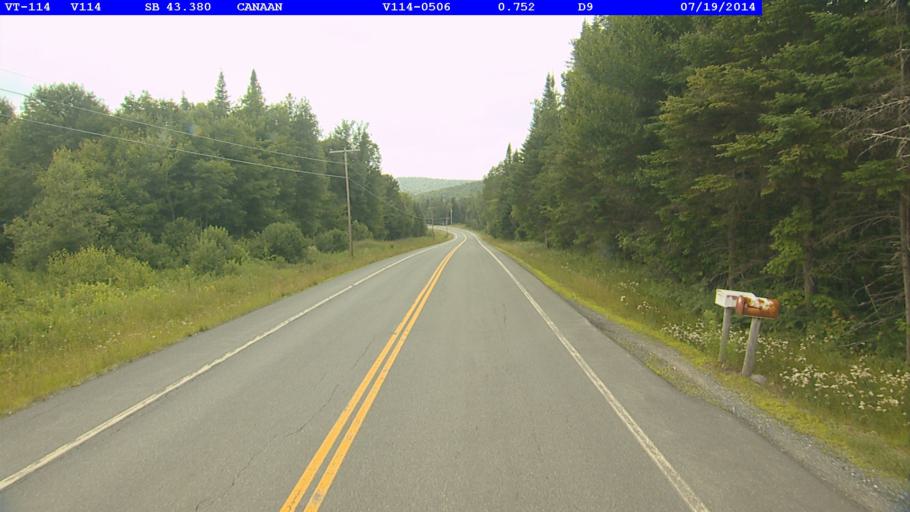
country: CA
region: Quebec
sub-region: Estrie
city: Coaticook
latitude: 45.0061
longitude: -71.6784
